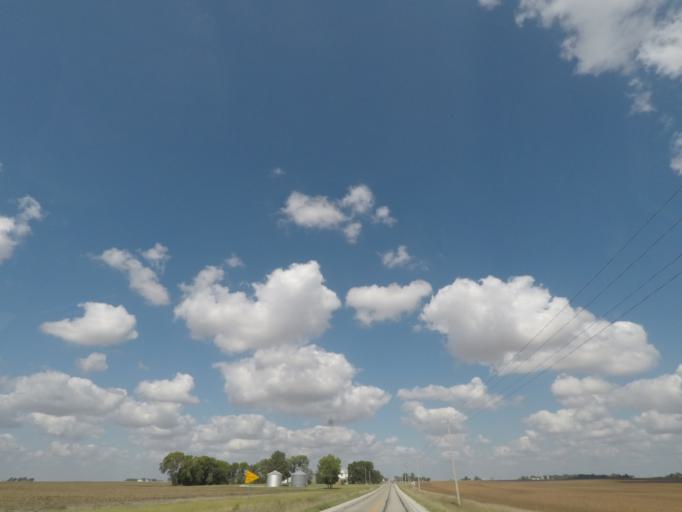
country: US
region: Iowa
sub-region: Story County
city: Nevada
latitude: 42.0509
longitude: -93.4063
